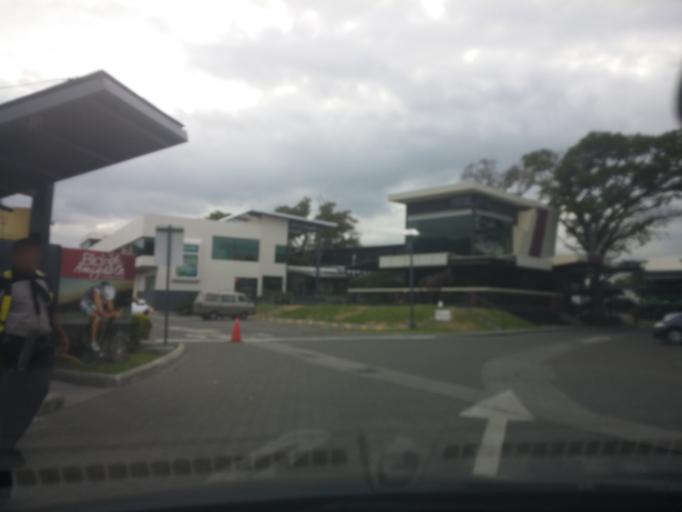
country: CR
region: San Jose
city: Santa Ana
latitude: 9.9530
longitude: -84.1951
